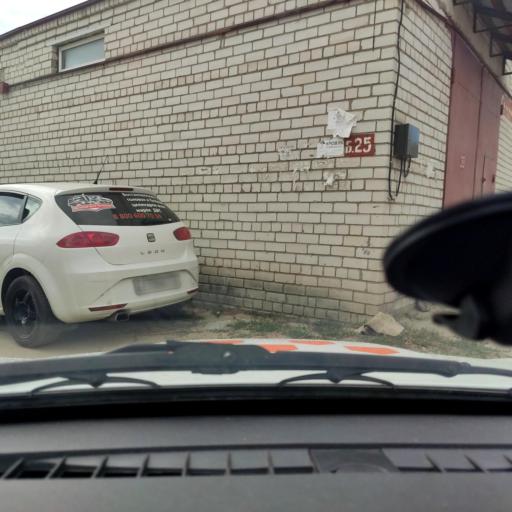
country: RU
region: Voronezj
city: Pridonskoy
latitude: 51.6402
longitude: 39.1189
